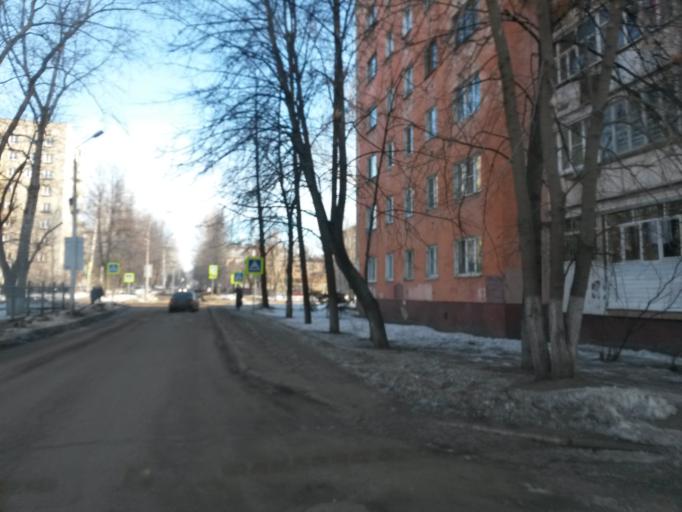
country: RU
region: Jaroslavl
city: Yaroslavl
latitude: 57.6229
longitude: 39.8533
